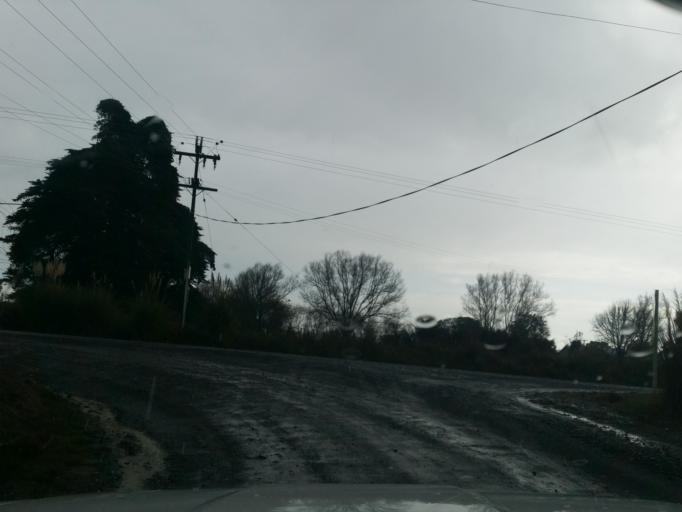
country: NZ
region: Northland
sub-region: Whangarei
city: Maungatapere
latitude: -36.0503
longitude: 174.1736
